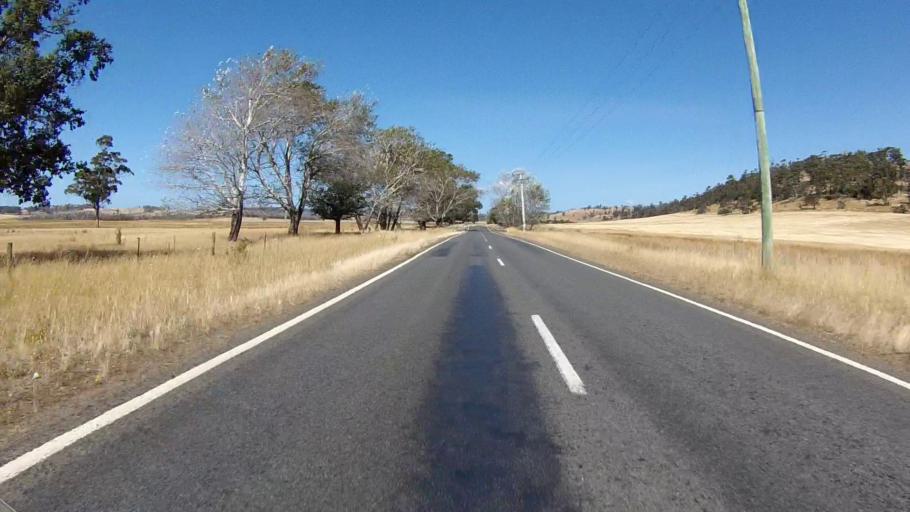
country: AU
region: Tasmania
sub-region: Sorell
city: Sorell
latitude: -42.4728
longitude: 147.9264
